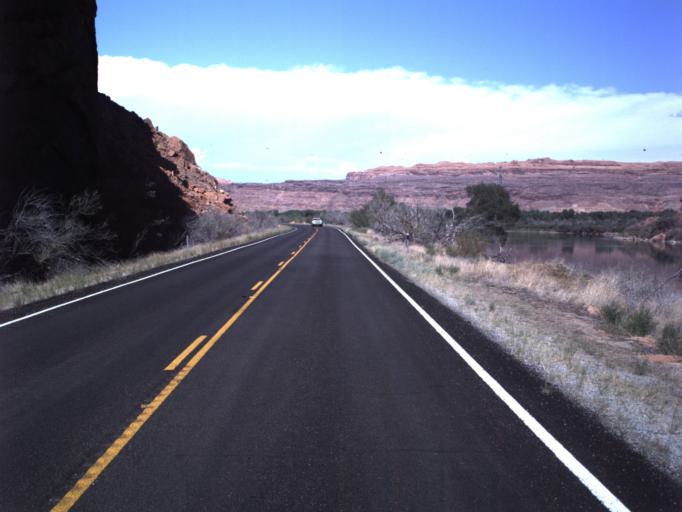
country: US
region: Utah
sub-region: Grand County
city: Moab
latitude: 38.5681
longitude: -109.5813
